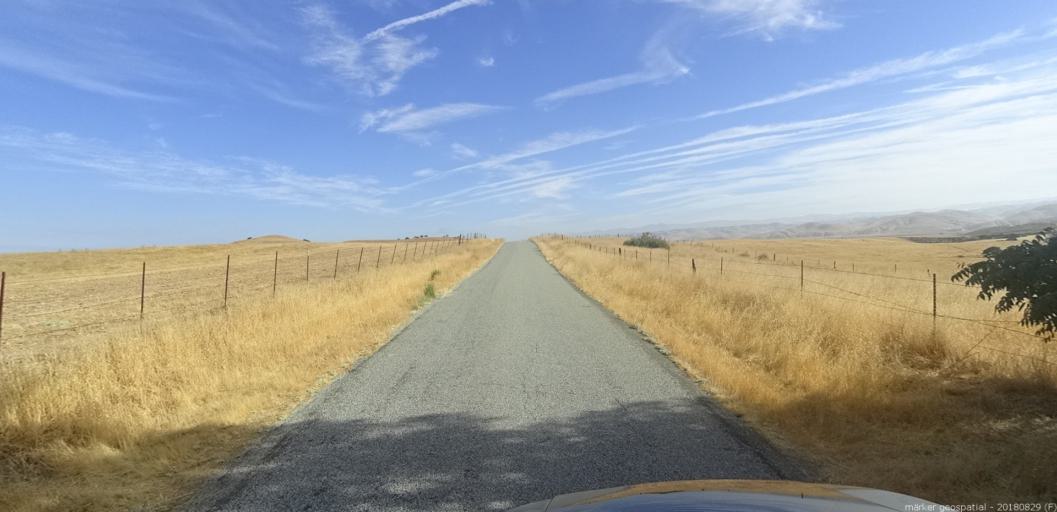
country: US
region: California
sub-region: Monterey County
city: King City
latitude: 36.0216
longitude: -120.9484
